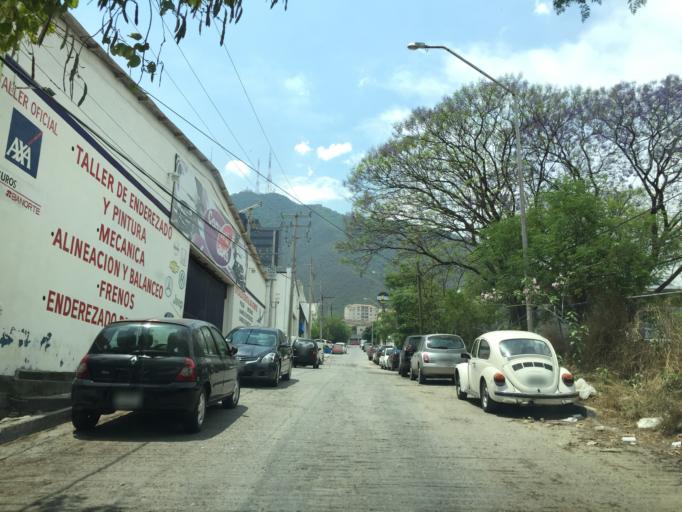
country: MX
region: Nuevo Leon
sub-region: Monterrey
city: Monterrey
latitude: 25.6367
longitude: -100.3108
